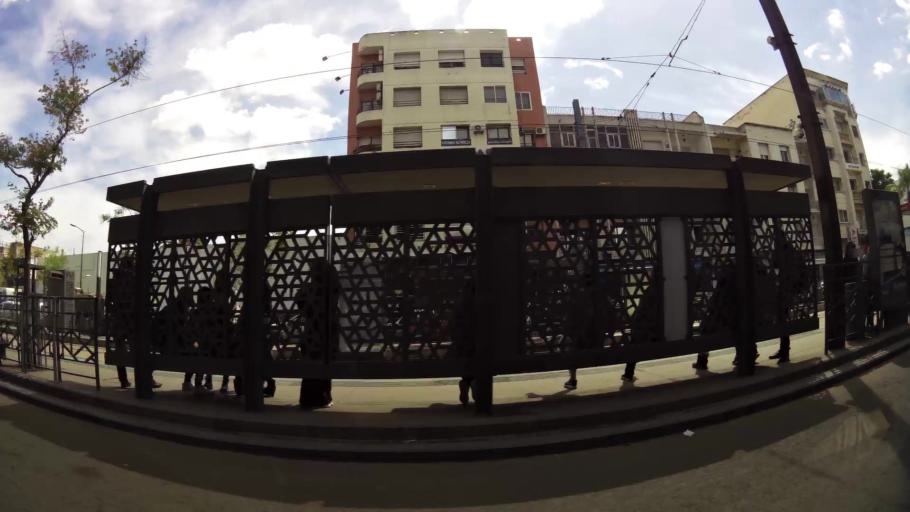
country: MA
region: Grand Casablanca
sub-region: Casablanca
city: Casablanca
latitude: 33.5710
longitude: -7.6260
